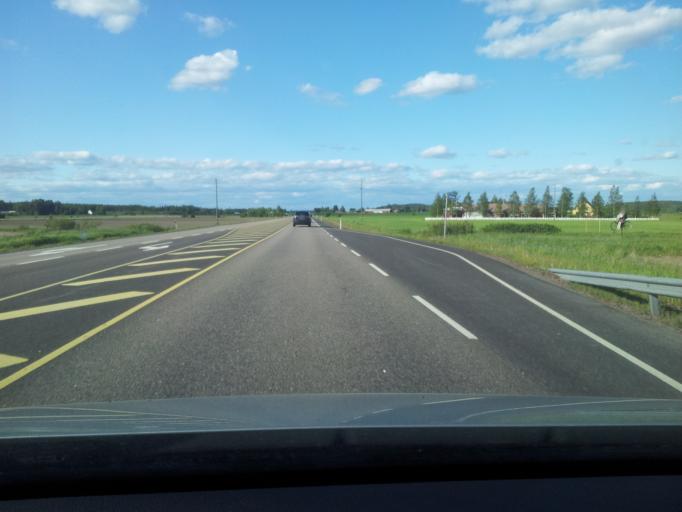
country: FI
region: Kymenlaakso
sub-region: Kouvola
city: Elimaeki
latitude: 60.7440
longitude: 26.4496
